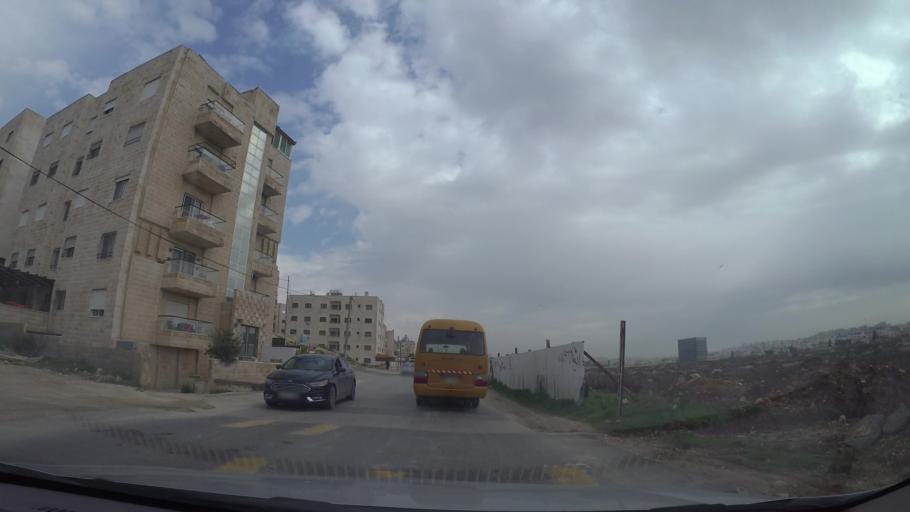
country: JO
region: Amman
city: Umm as Summaq
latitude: 31.8960
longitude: 35.8460
